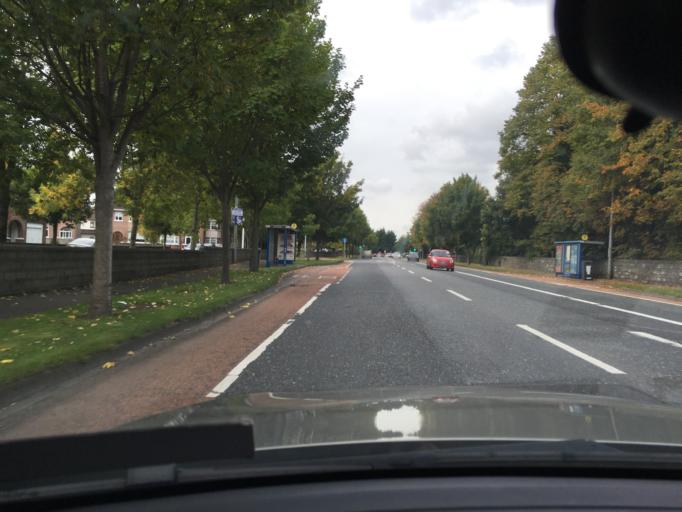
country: IE
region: Leinster
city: Chapelizod
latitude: 53.3705
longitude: -6.3272
